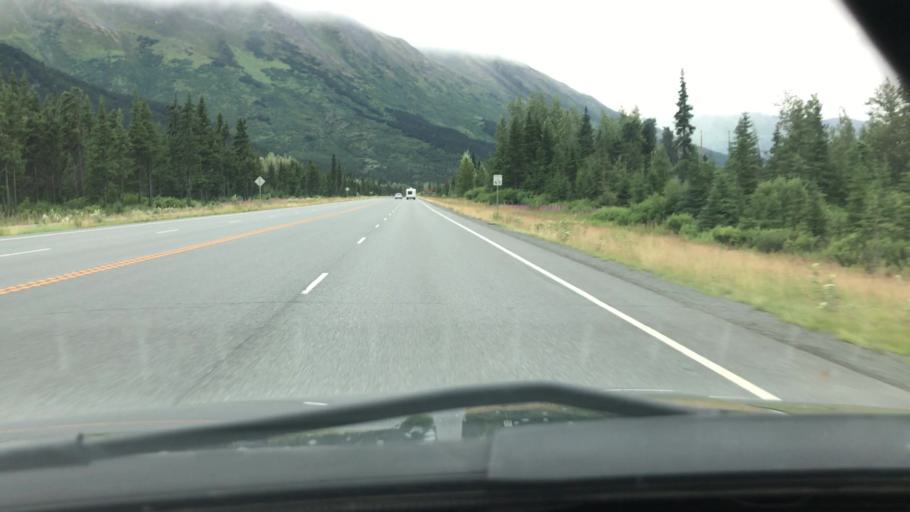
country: US
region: Alaska
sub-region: Anchorage Municipality
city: Girdwood
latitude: 60.7282
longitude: -149.3102
